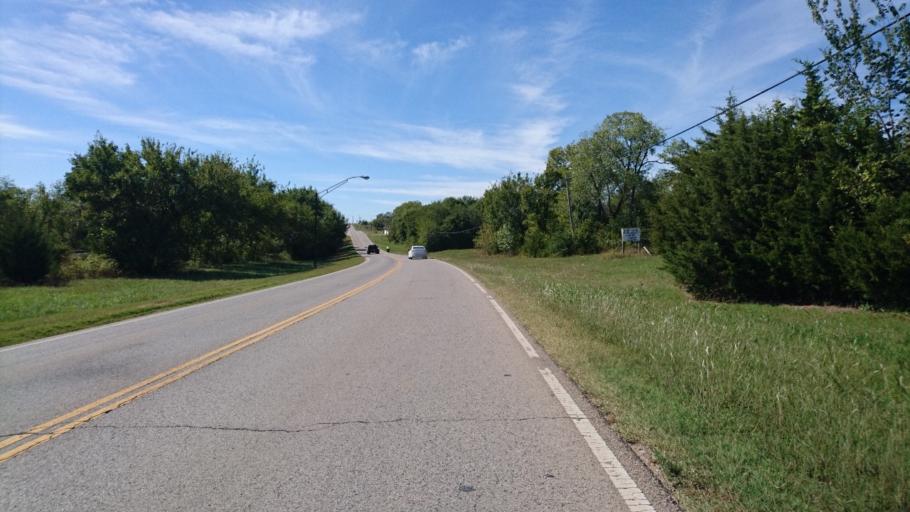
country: US
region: Oklahoma
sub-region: Lincoln County
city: Stroud
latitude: 35.7511
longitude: -96.6726
